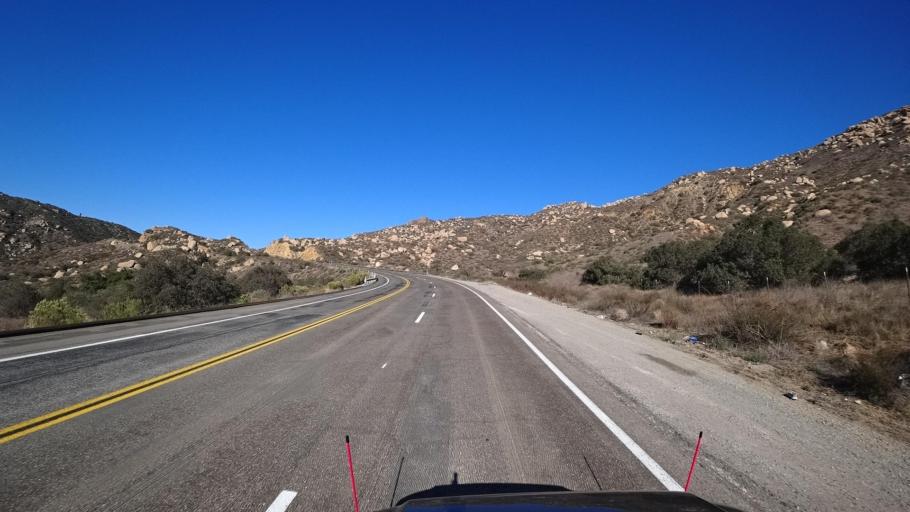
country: MX
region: Baja California
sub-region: Tecate
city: Lomas de Santa Anita
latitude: 32.6152
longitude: -116.7178
